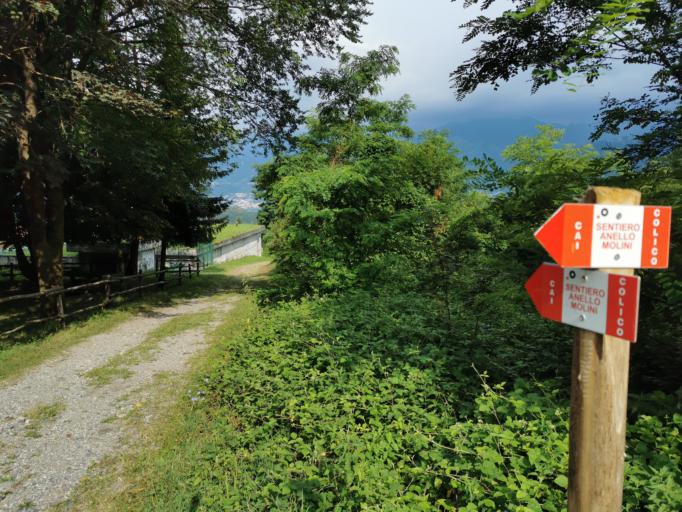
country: IT
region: Lombardy
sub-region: Provincia di Lecco
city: Colico Piano
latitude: 46.1229
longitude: 9.3894
